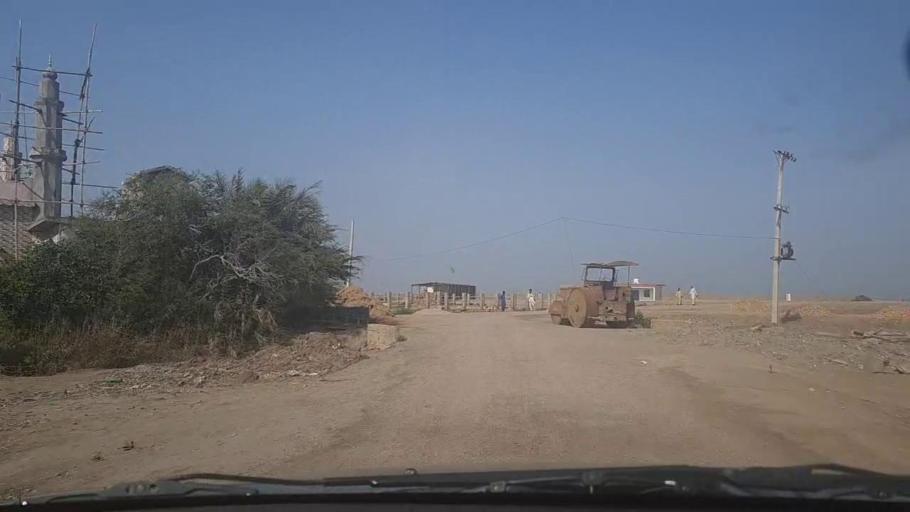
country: PK
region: Sindh
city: Keti Bandar
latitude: 24.1830
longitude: 67.5033
